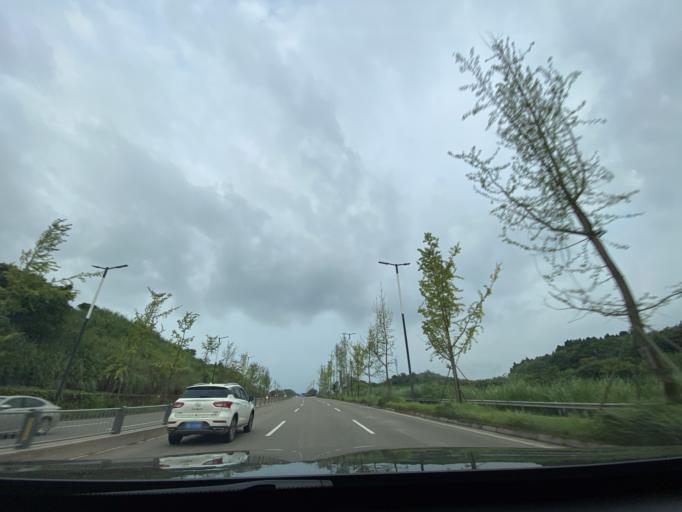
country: CN
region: Sichuan
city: Jiancheng
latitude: 30.4881
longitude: 104.4743
